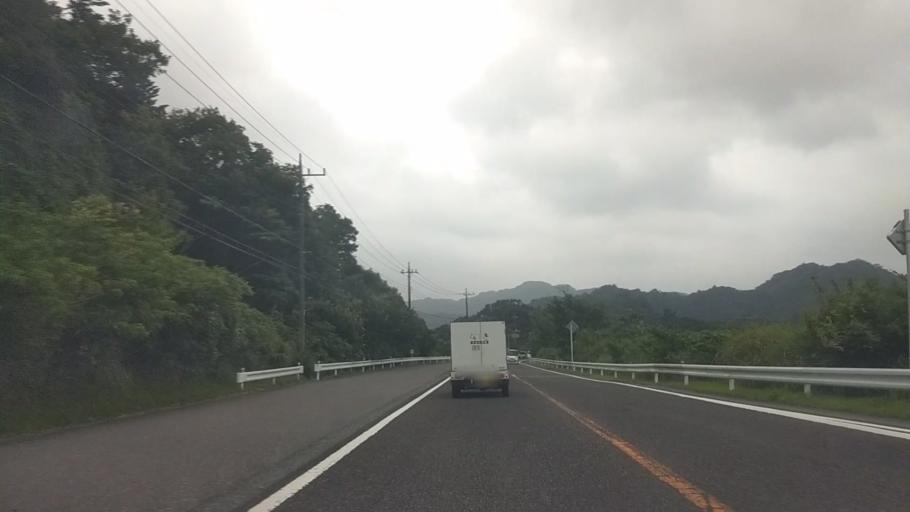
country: JP
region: Chiba
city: Kawaguchi
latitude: 35.1615
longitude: 140.0629
